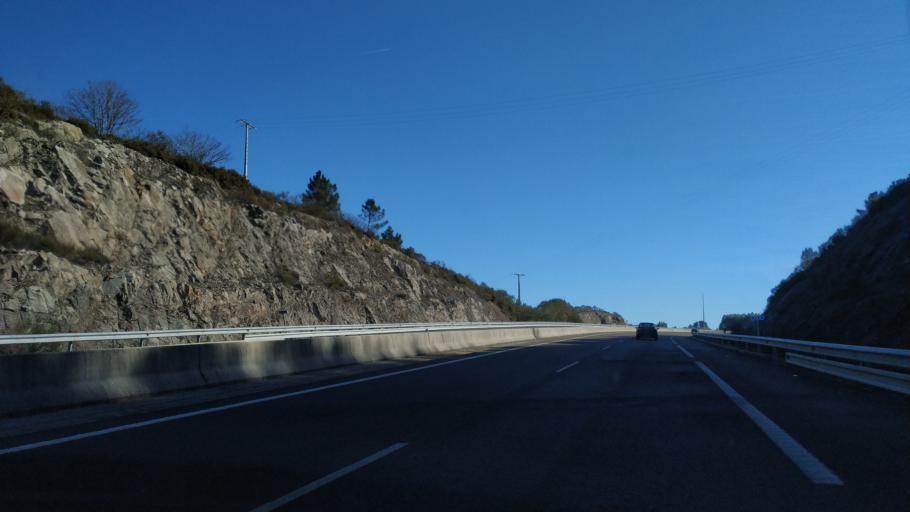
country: ES
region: Galicia
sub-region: Provincia de Pontevedra
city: Dozon
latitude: 42.5655
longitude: -8.0486
